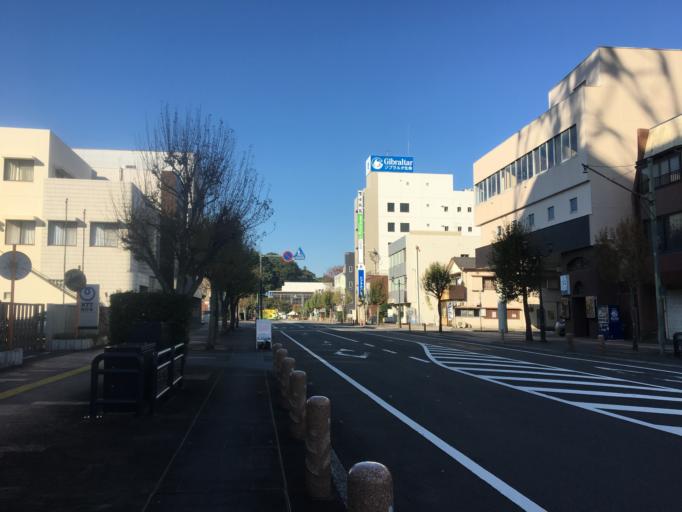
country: JP
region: Miyazaki
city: Nobeoka
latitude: 32.5819
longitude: 131.6671
